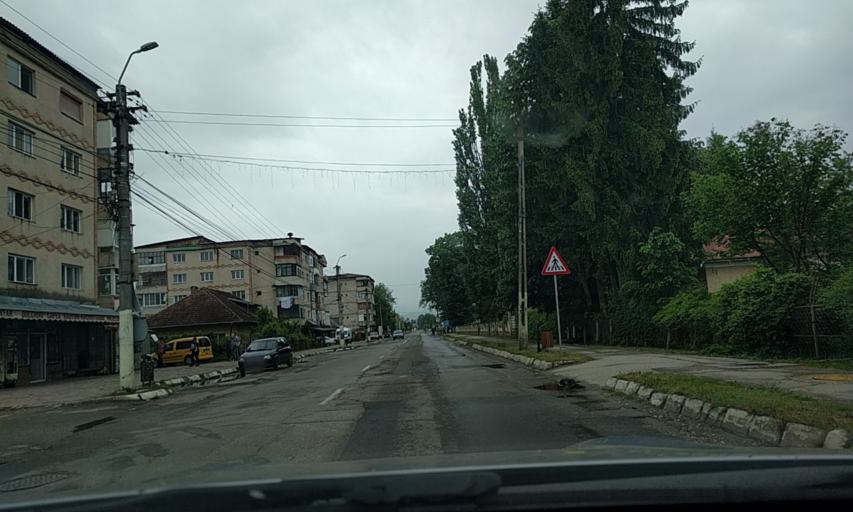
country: RO
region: Dambovita
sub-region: Oras Pucioasa
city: Glodeni
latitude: 45.0591
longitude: 25.4386
